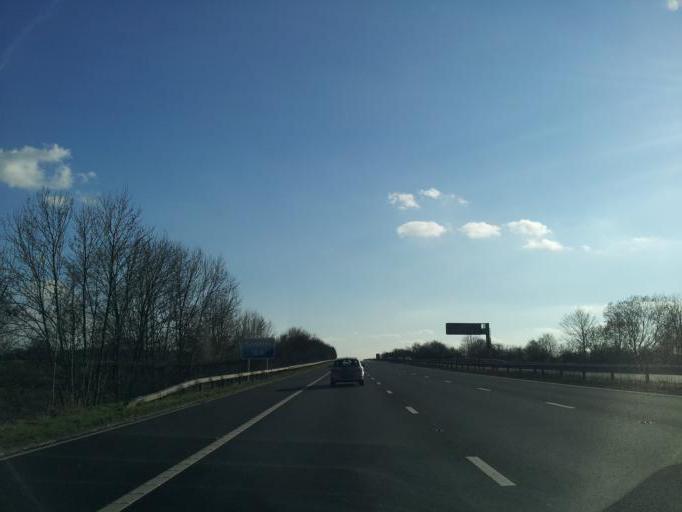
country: GB
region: England
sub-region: Devon
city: Uffculme
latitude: 50.8991
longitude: -3.3719
